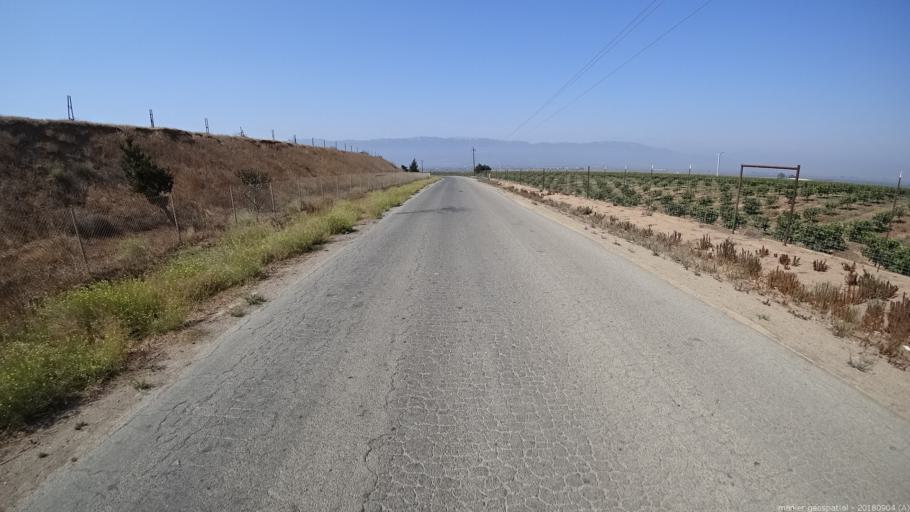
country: US
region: California
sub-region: Monterey County
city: Gonzales
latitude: 36.5319
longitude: -121.4098
